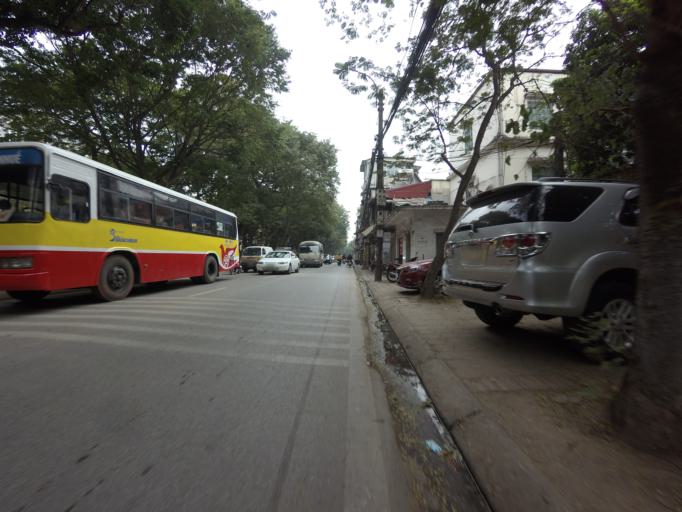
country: VN
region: Ha Noi
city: Hanoi
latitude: 21.0420
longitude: 105.8347
